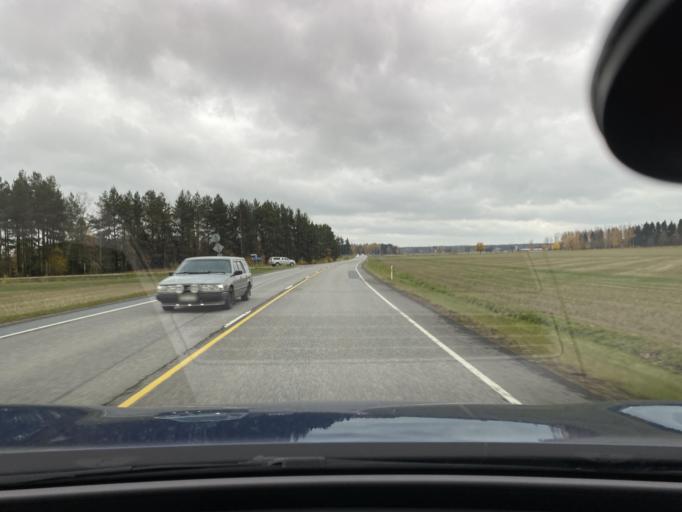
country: FI
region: Satakunta
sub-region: Rauma
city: Kiukainen
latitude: 61.1905
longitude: 22.0602
